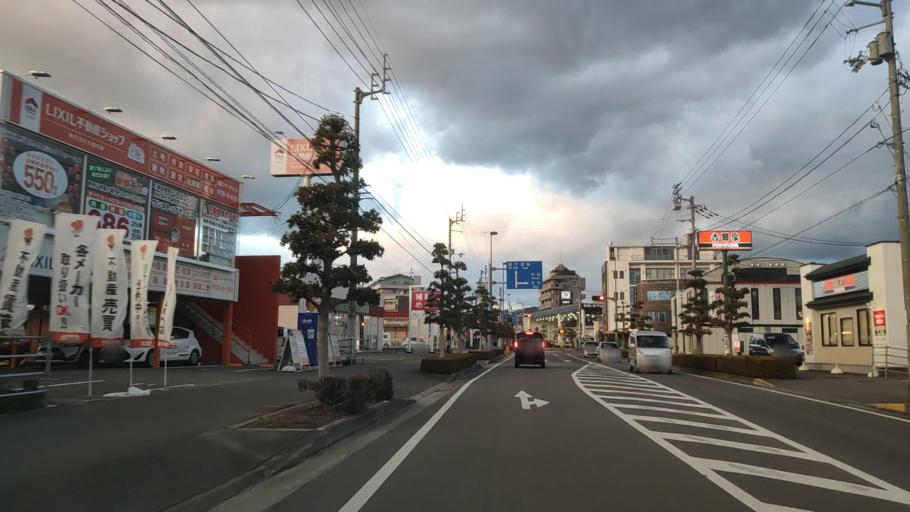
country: JP
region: Ehime
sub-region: Shikoku-chuo Shi
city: Matsuyama
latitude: 33.8364
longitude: 132.7869
